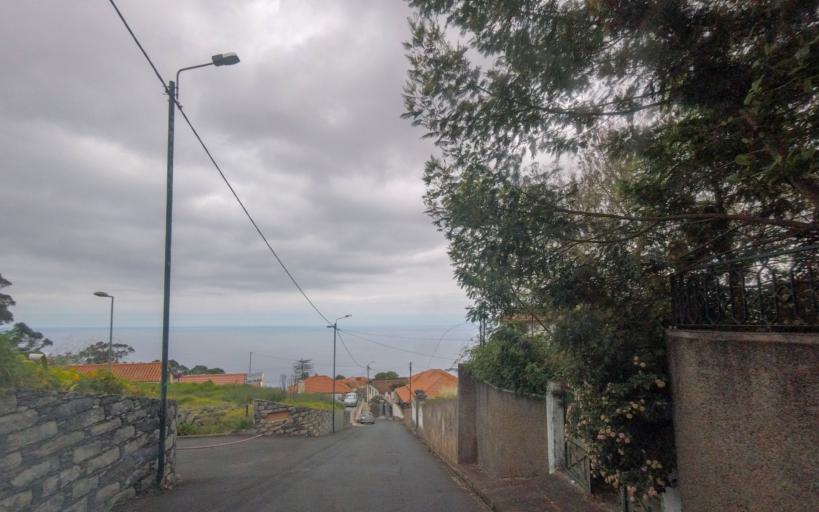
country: PT
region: Madeira
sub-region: Funchal
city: Nossa Senhora do Monte
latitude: 32.6600
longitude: -16.8795
